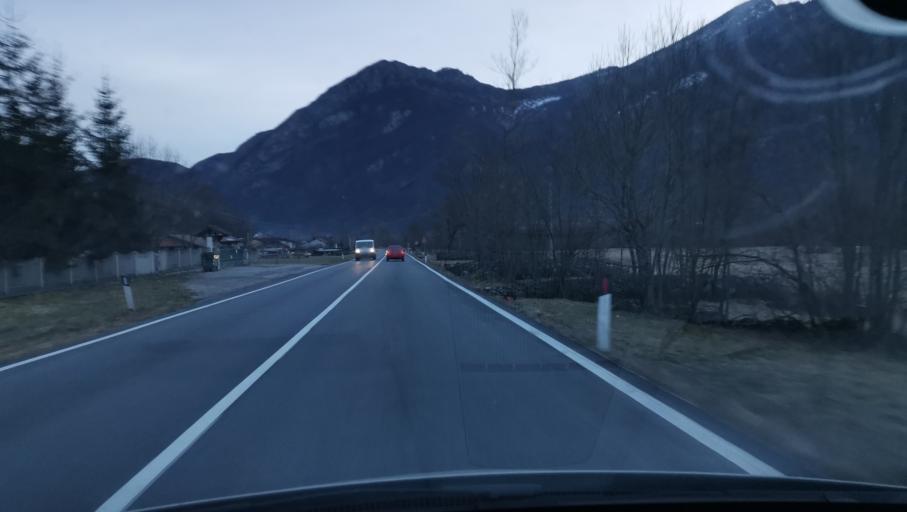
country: IT
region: Piedmont
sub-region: Provincia di Cuneo
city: Moiola
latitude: 44.3106
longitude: 7.3636
